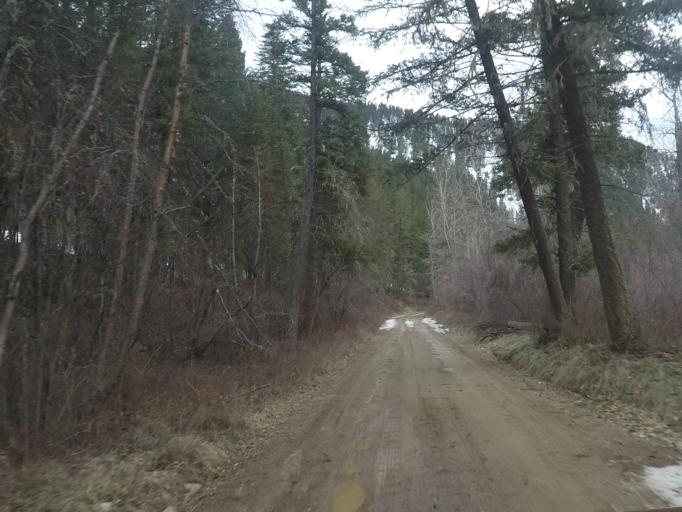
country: US
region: Montana
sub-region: Missoula County
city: Clinton
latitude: 46.5735
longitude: -113.6848
